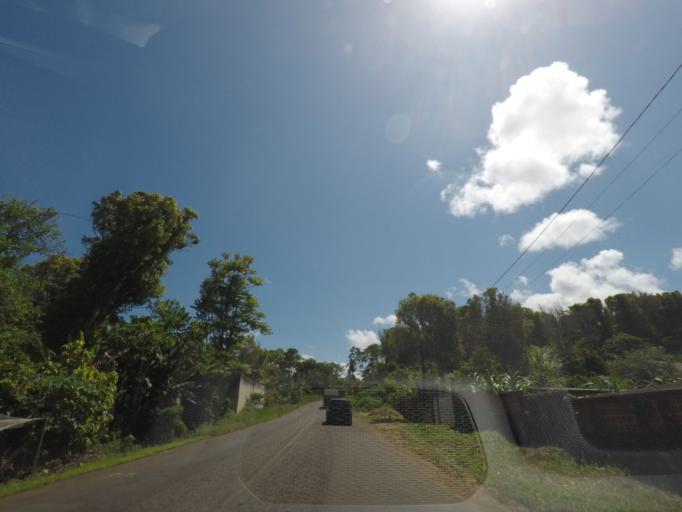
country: BR
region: Bahia
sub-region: Valenca
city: Valenca
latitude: -13.4439
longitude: -39.0821
